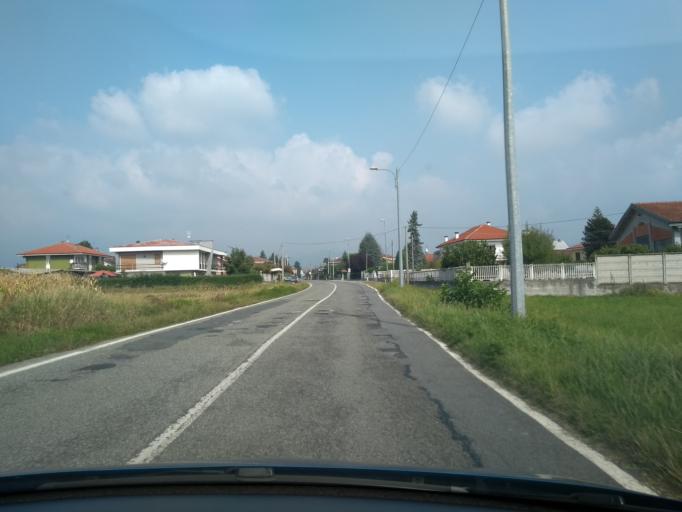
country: IT
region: Piedmont
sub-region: Provincia di Torino
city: Oglianico
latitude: 45.3518
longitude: 7.6922
